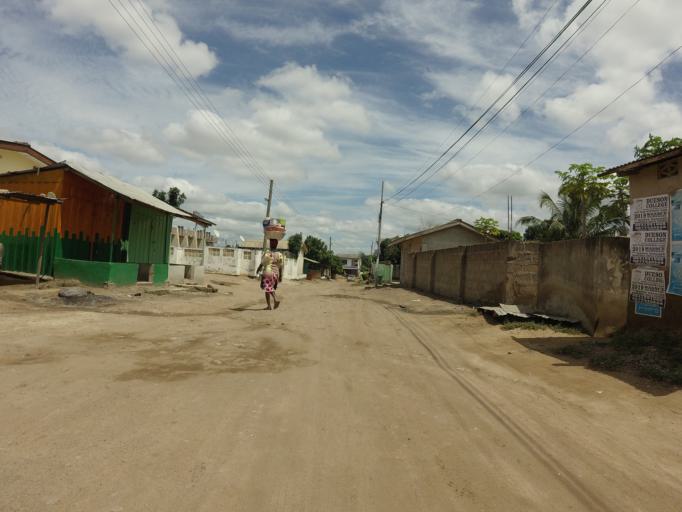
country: GH
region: Central
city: Kasoa
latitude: 5.5417
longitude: -0.4021
